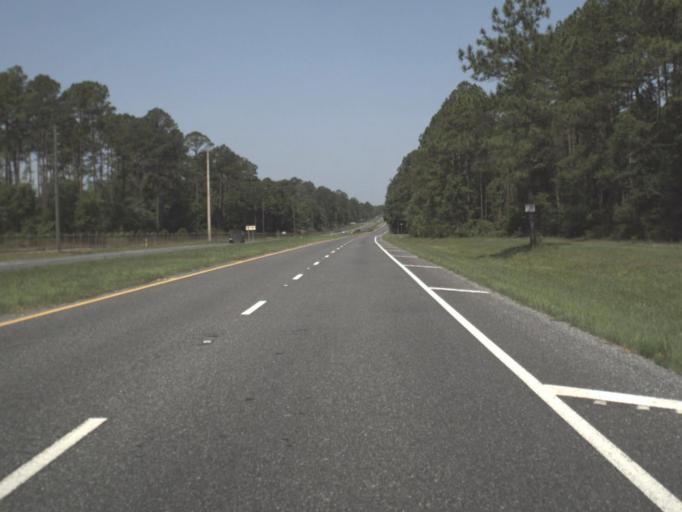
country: US
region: Florida
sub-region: Clay County
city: Middleburg
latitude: 29.9817
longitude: -81.9623
